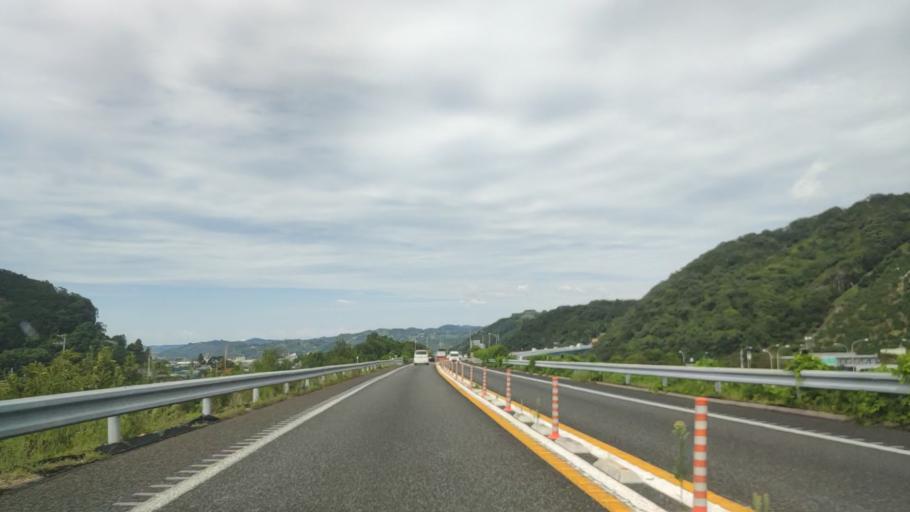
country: JP
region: Wakayama
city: Gobo
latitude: 34.0084
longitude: 135.1915
